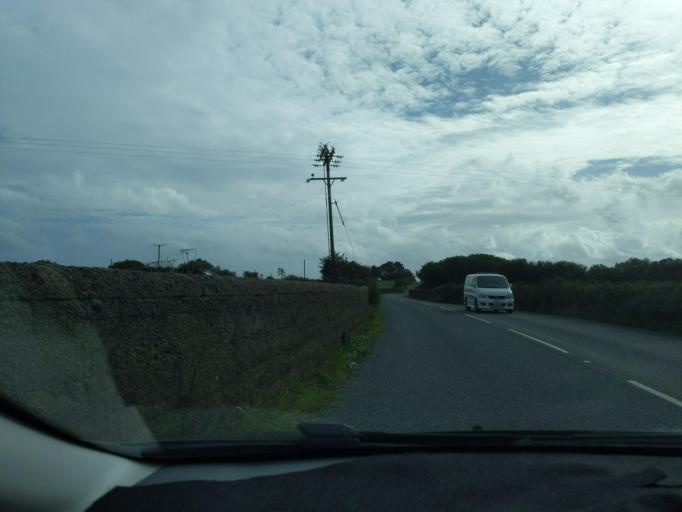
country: GB
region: England
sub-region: Cornwall
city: Mevagissey
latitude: 50.2707
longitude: -4.8294
